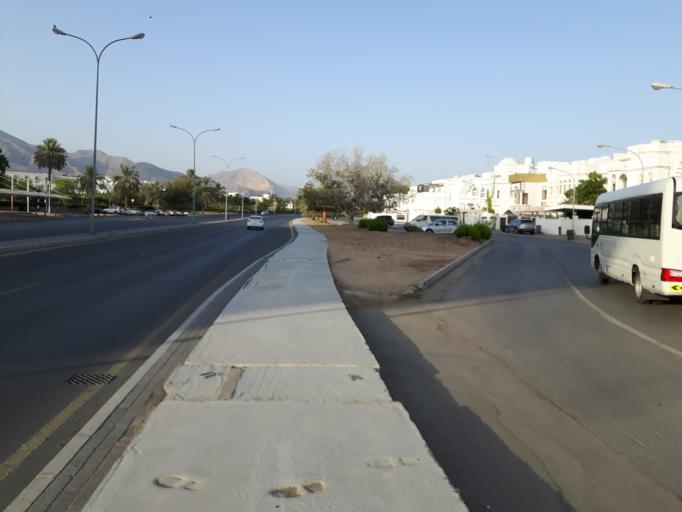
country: OM
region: Muhafazat Masqat
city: Bawshar
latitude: 23.6068
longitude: 58.4529
